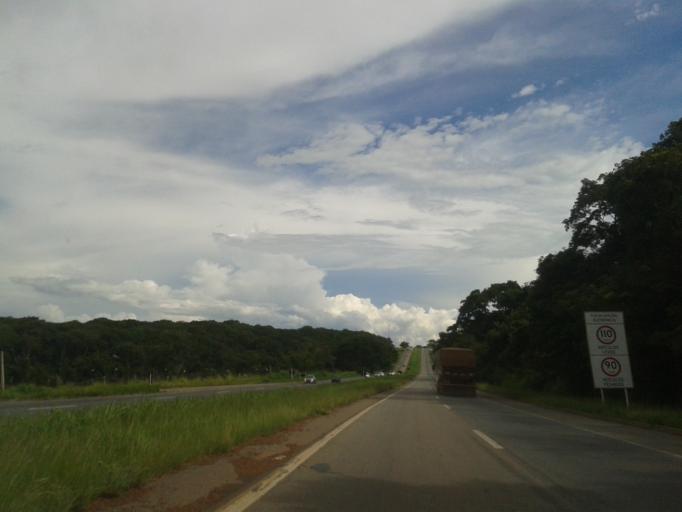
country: BR
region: Goias
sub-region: Hidrolandia
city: Hidrolandia
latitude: -16.9785
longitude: -49.2299
